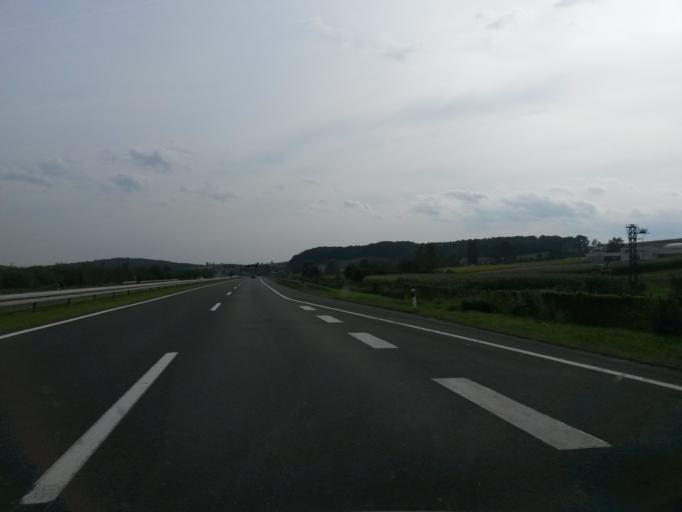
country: HR
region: Varazdinska
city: Remetinec
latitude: 46.0964
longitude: 16.2836
